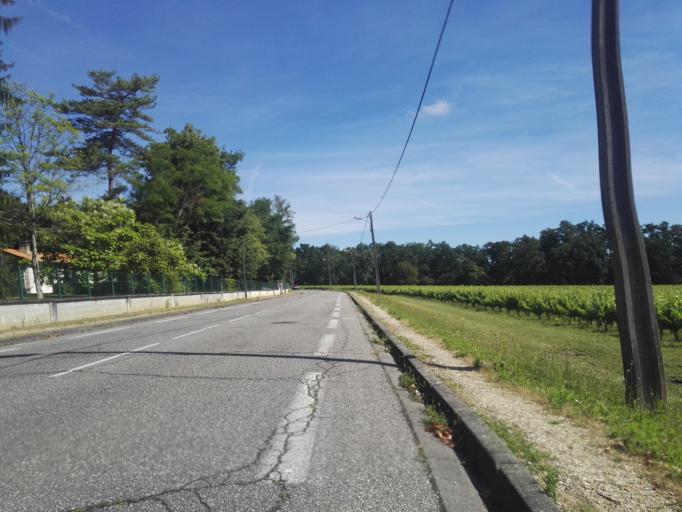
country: FR
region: Aquitaine
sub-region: Departement de la Gironde
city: Leognan
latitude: 44.7461
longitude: -0.5870
